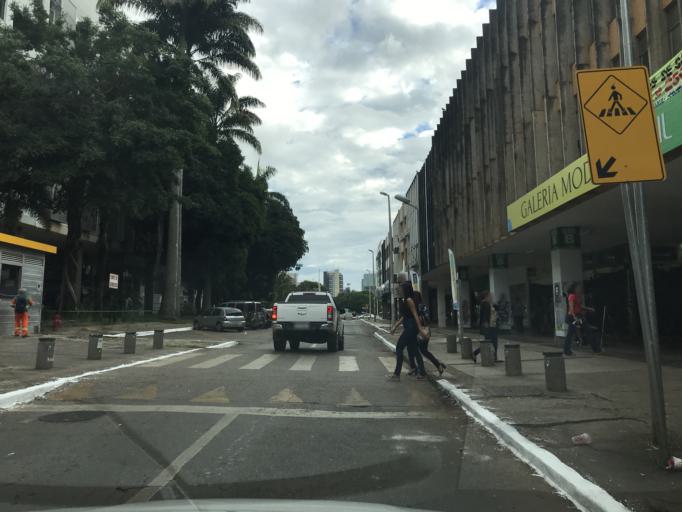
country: BR
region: Federal District
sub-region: Brasilia
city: Brasilia
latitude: -15.7979
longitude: -47.8883
